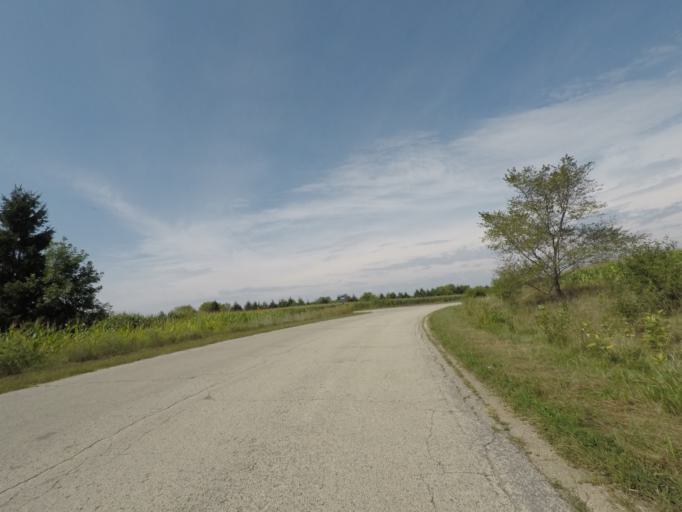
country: US
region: Wisconsin
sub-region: Jefferson County
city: Fort Atkinson
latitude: 42.8933
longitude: -88.8717
